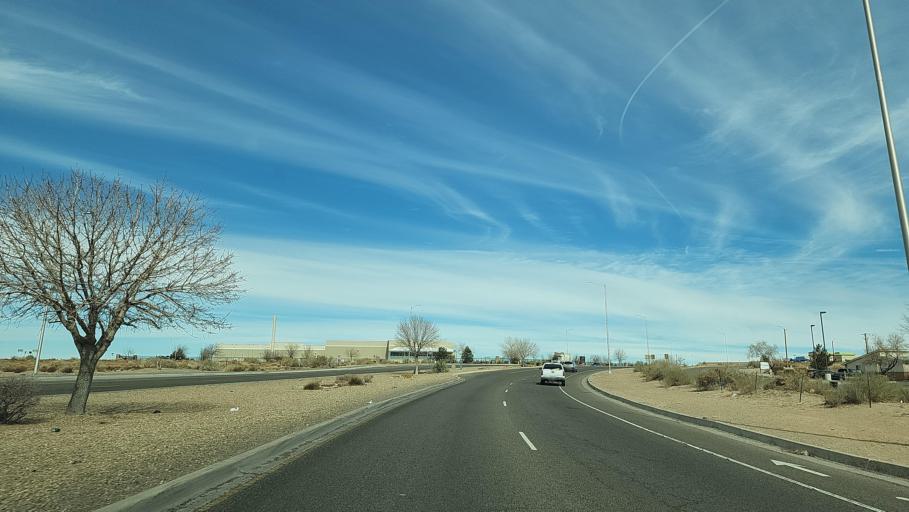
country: US
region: New Mexico
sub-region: Bernalillo County
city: Albuquerque
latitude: 35.0745
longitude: -106.7135
